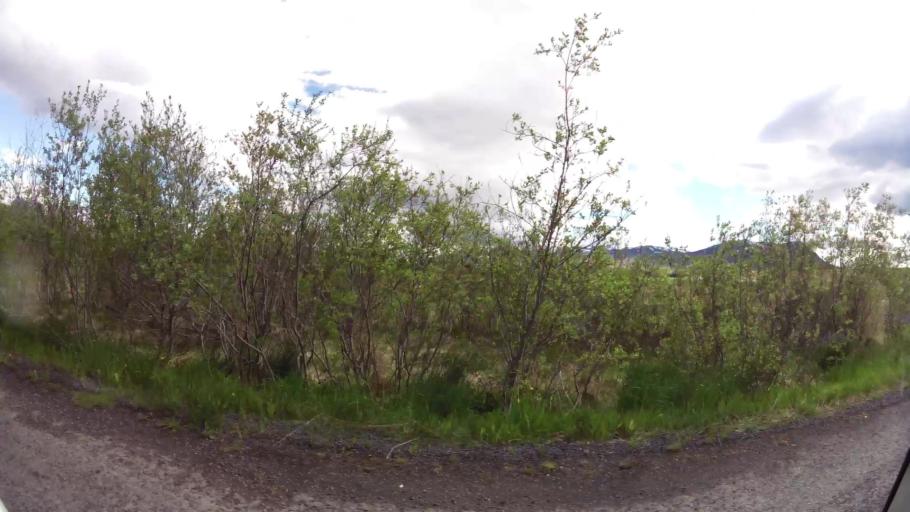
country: IS
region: Northwest
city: Saudarkrokur
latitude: 65.5506
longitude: -19.4546
